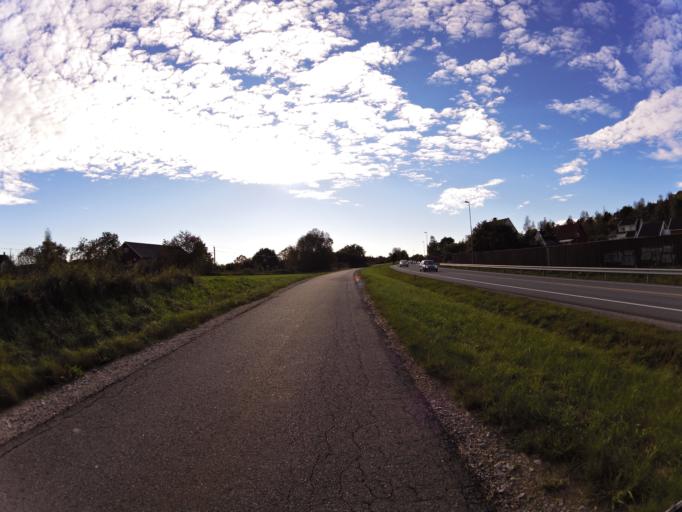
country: NO
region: Ostfold
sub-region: Sarpsborg
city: Sarpsborg
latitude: 59.2711
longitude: 11.0725
